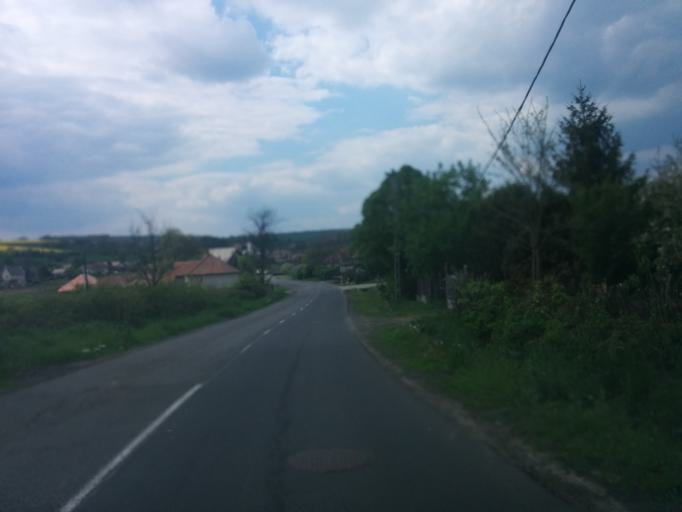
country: HU
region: Nograd
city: Palotas
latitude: 47.8220
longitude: 19.5909
